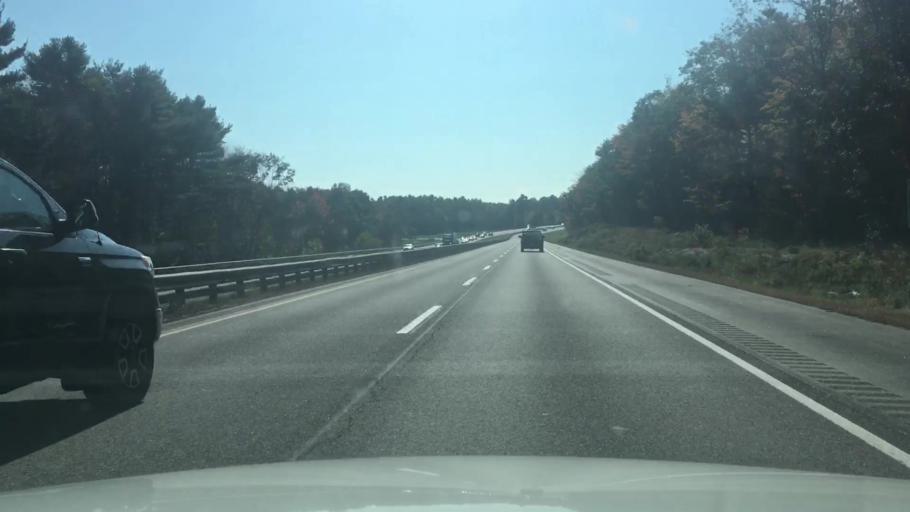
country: US
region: Maine
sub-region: Cumberland County
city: Freeport
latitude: 43.8820
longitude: -70.0830
